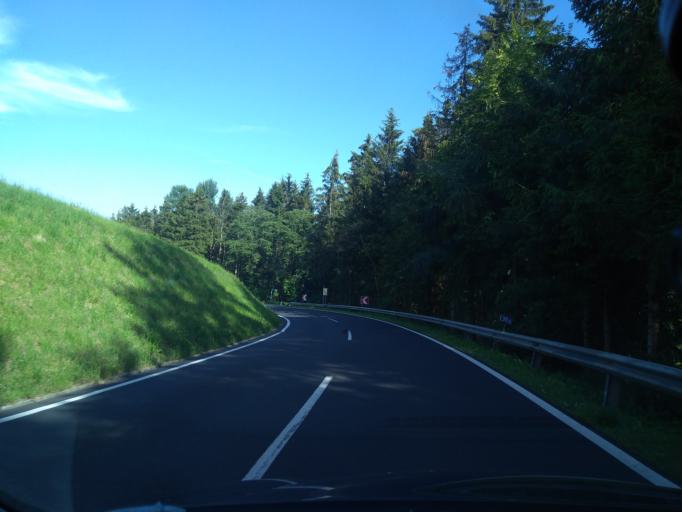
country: AT
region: Styria
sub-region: Politischer Bezirk Graz-Umgebung
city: Semriach
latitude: 47.2660
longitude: 15.4399
